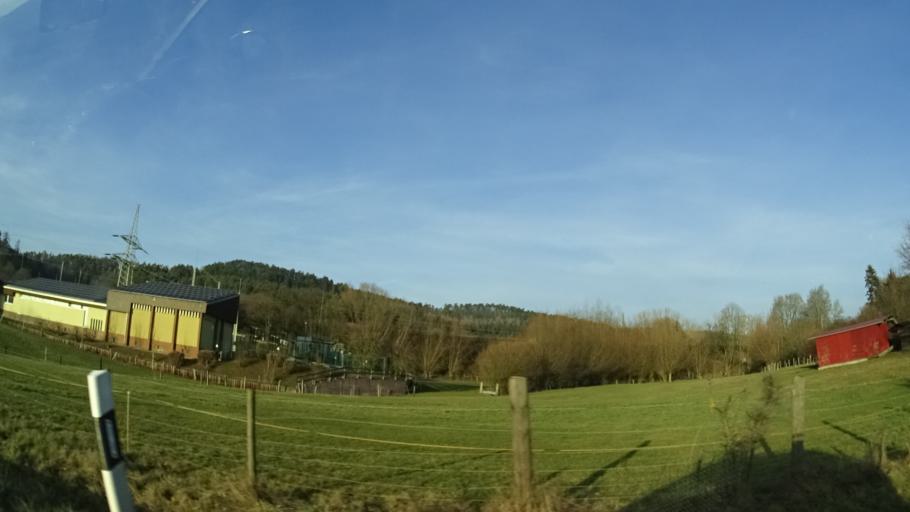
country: DE
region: Bavaria
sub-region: Regierungsbezirk Unterfranken
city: Zeitlofs
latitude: 50.3166
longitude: 9.6136
